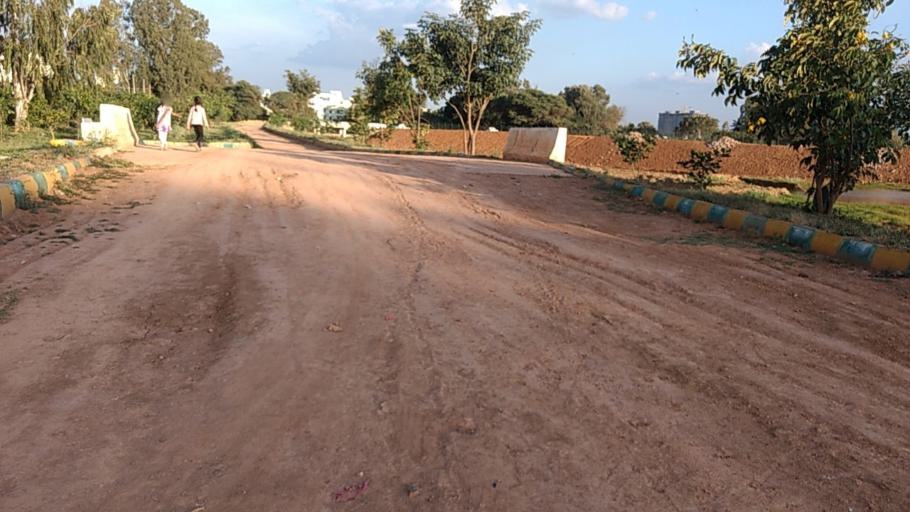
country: IN
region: Karnataka
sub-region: Bangalore Urban
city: Yelahanka
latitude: 13.0639
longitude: 77.5661
